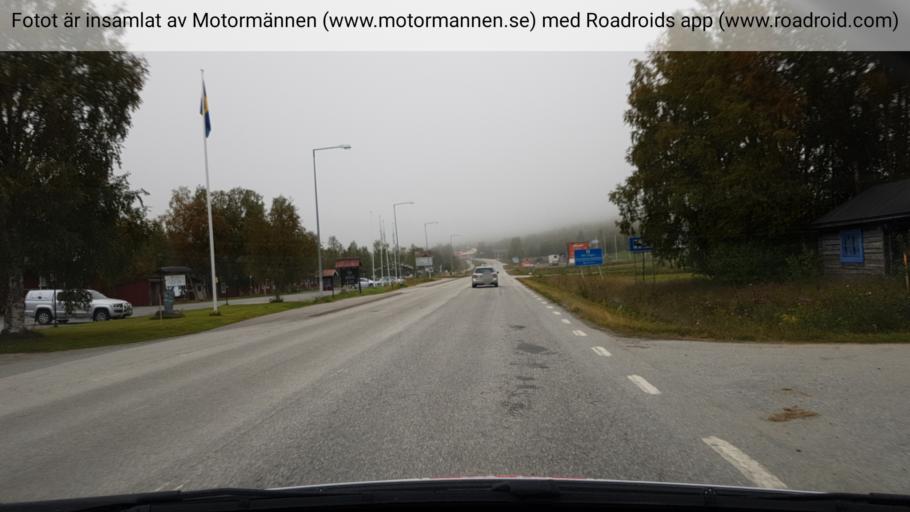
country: NO
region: Nordland
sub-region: Rana
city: Mo i Rana
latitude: 65.8129
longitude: 15.0881
